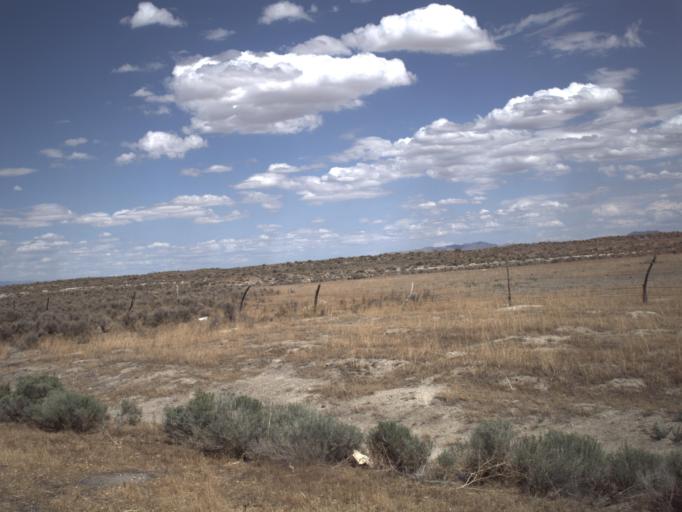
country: US
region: Utah
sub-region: Millard County
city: Delta
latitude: 39.2990
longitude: -112.4709
